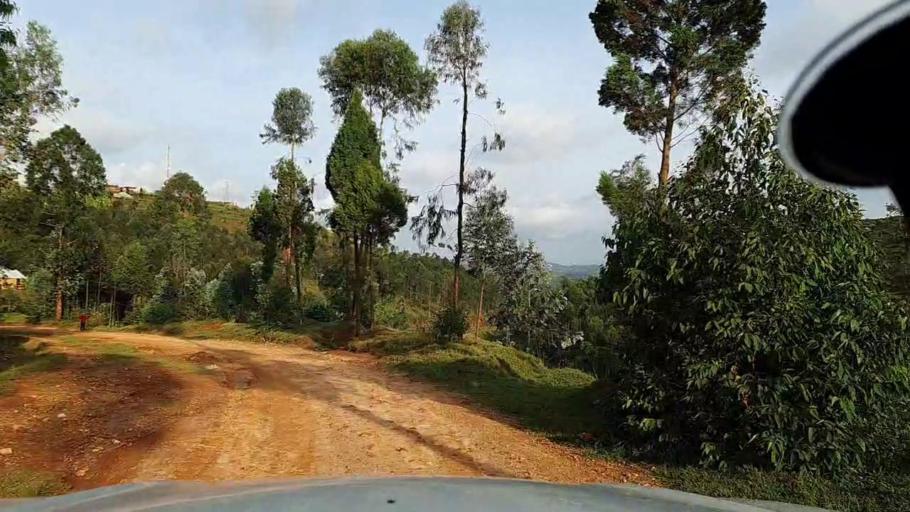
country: RW
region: Southern Province
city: Gitarama
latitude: -2.1861
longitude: 29.5690
